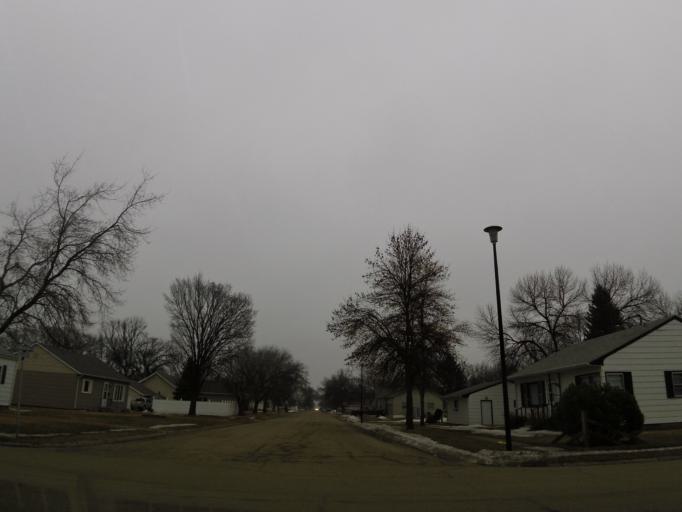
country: US
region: North Dakota
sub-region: Walsh County
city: Grafton
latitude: 48.4146
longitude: -97.4189
